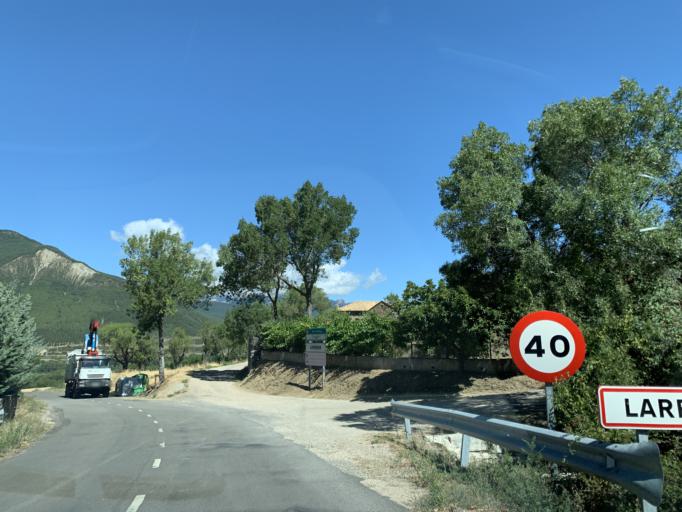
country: ES
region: Aragon
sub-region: Provincia de Huesca
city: Sabinanigo
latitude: 42.5510
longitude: -0.3165
